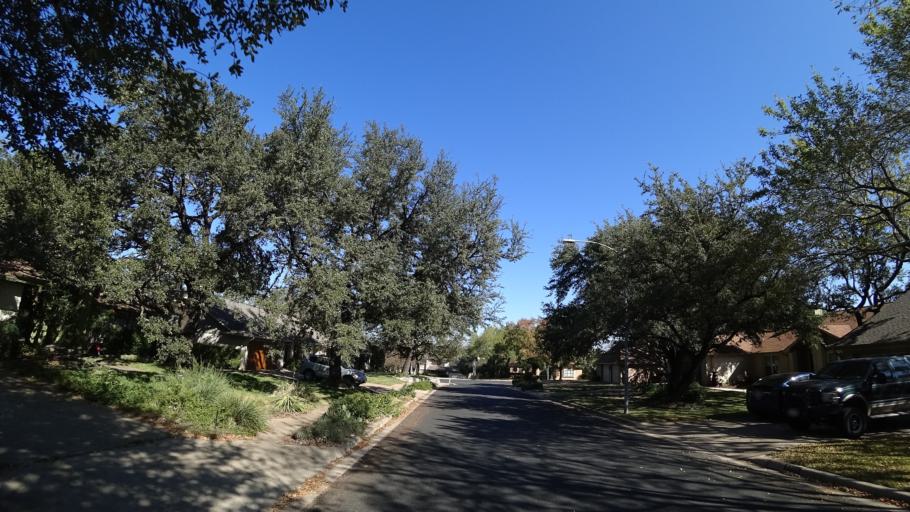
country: US
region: Texas
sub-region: Williamson County
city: Jollyville
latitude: 30.4182
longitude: -97.7639
